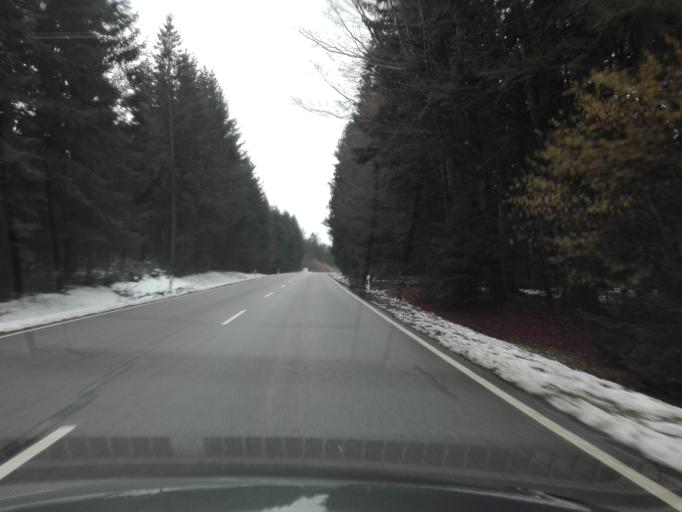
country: DE
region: Bavaria
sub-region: Lower Bavaria
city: Untergriesbach
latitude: 48.5764
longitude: 13.7072
